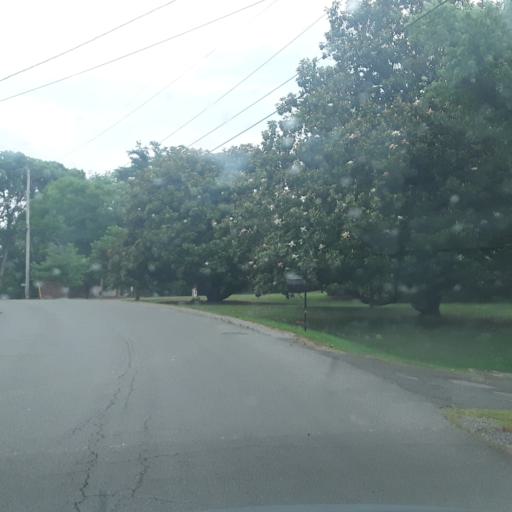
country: US
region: Tennessee
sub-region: Davidson County
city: Oak Hill
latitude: 36.0719
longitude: -86.7402
